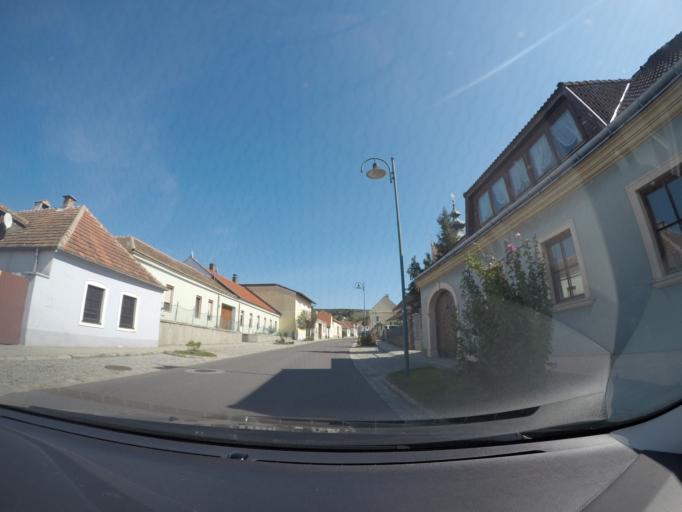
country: AT
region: Lower Austria
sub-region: Politischer Bezirk Bruck an der Leitha
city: Hof am Leithaberge
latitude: 47.9447
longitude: 16.5769
